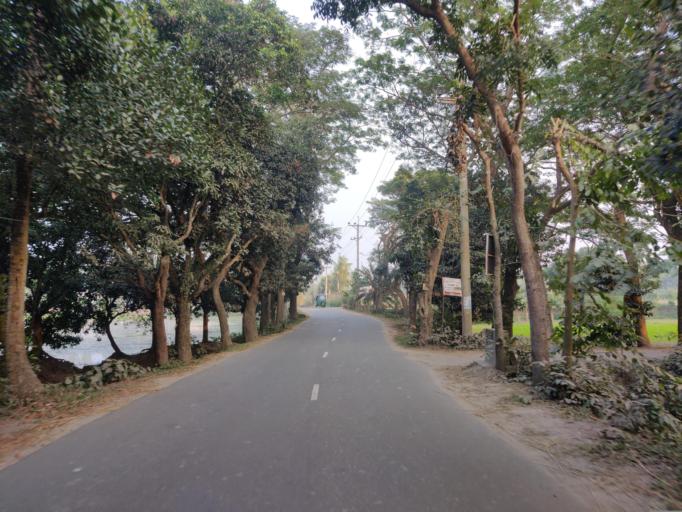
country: BD
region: Dhaka
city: Bajitpur
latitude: 24.1580
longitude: 90.7614
